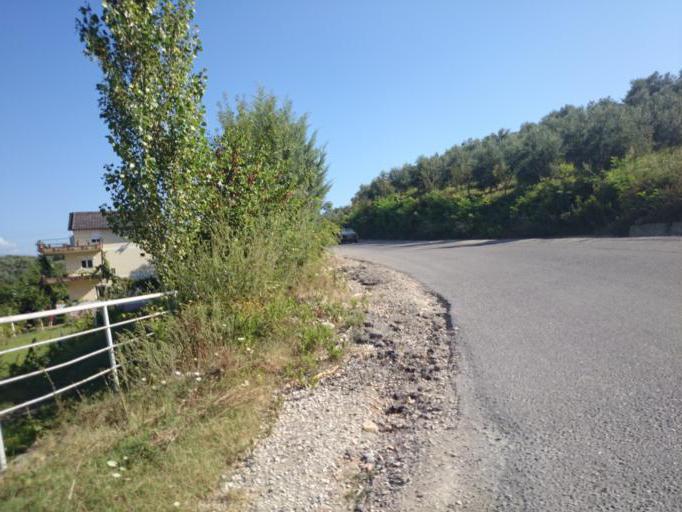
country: AL
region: Elbasan
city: Elbasan
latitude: 41.0892
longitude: 20.0995
